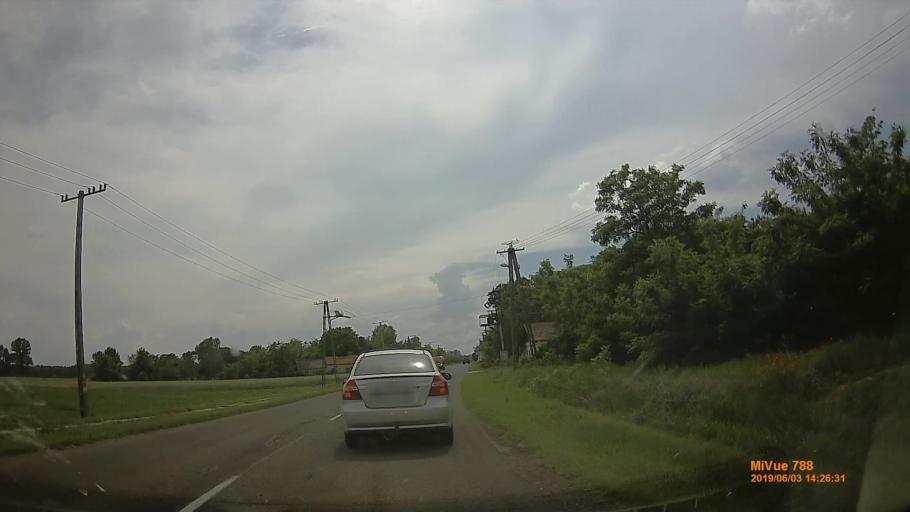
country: HU
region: Bacs-Kiskun
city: Tiszakecske
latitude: 46.9908
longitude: 20.1248
